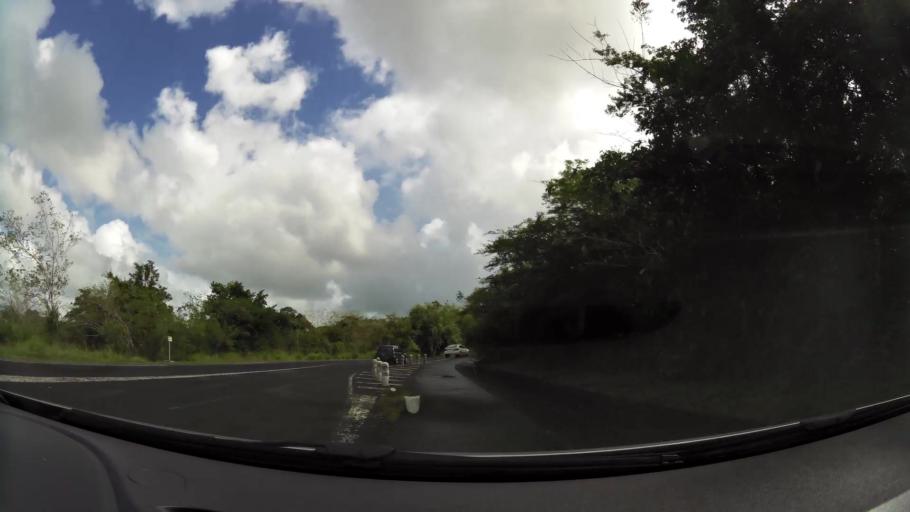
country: MQ
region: Martinique
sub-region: Martinique
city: Sainte-Luce
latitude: 14.4959
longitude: -60.9848
